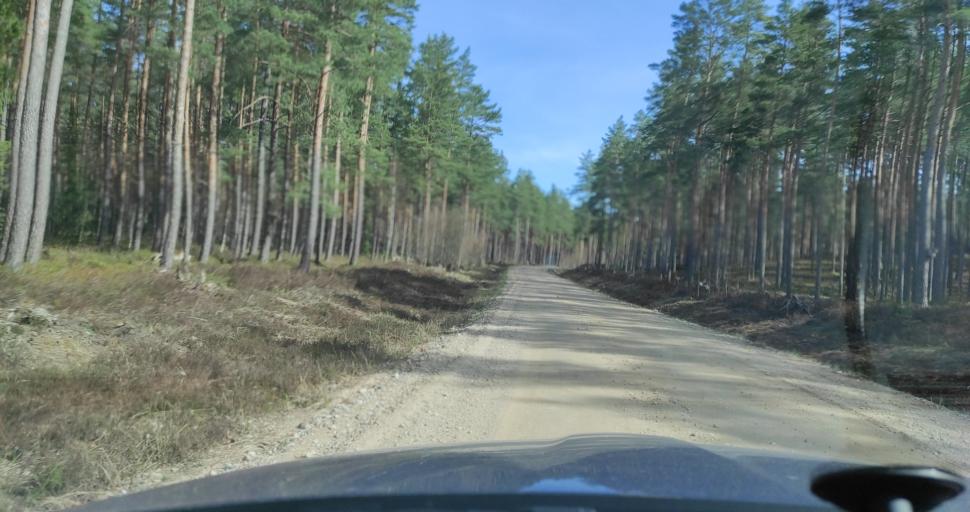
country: LV
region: Talsu Rajons
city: Stende
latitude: 57.2162
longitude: 22.2228
